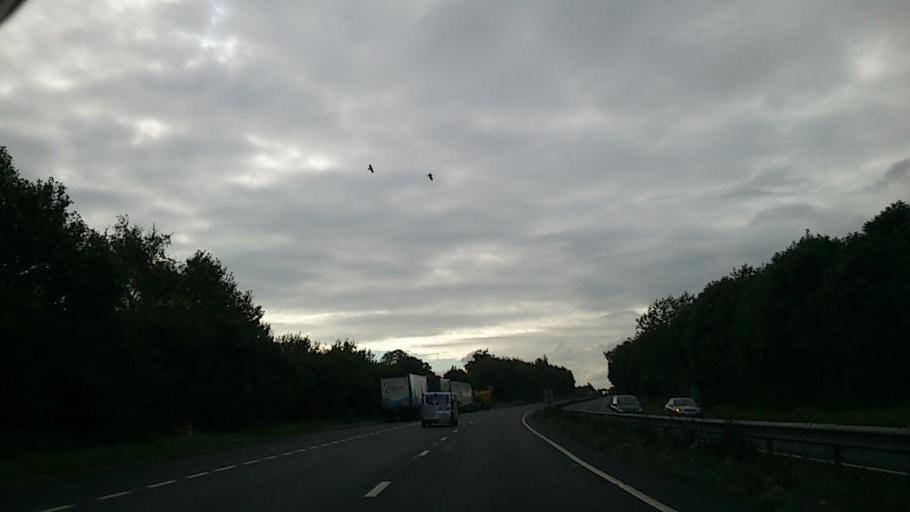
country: GB
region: England
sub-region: Shropshire
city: Great Hanwood
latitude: 52.7011
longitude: -2.8085
